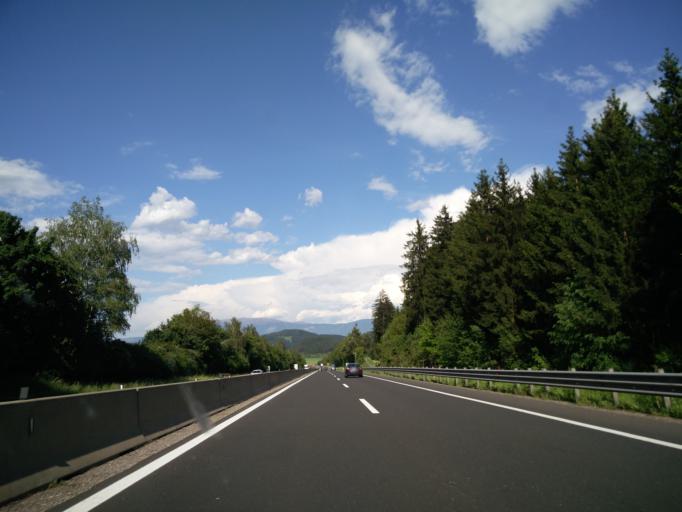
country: AT
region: Carinthia
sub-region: Politischer Bezirk Volkermarkt
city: Griffen
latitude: 46.6845
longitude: 14.6876
